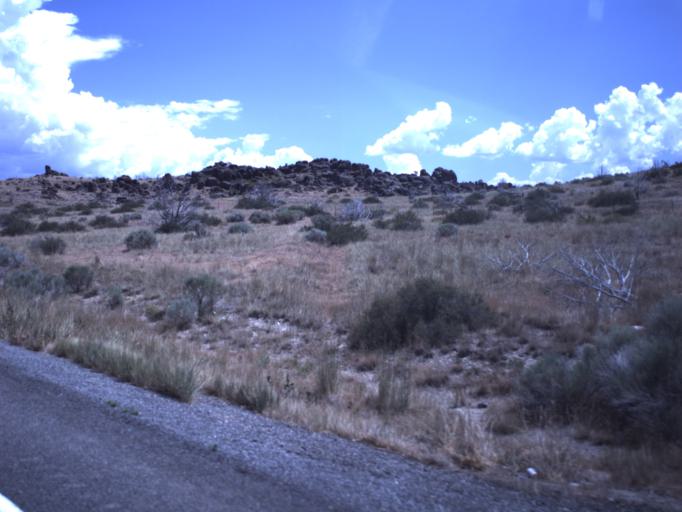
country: US
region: Utah
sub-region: Juab County
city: Nephi
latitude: 39.6533
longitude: -112.0751
